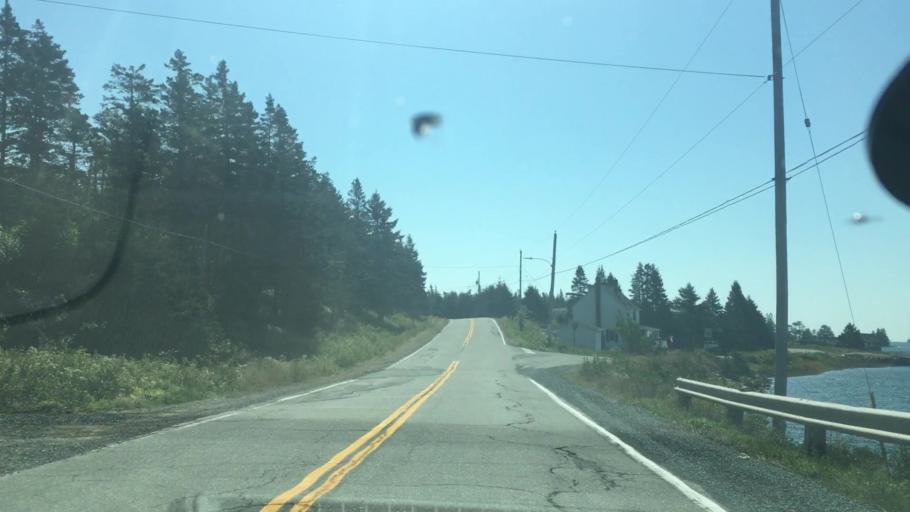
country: CA
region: Nova Scotia
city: New Glasgow
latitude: 44.9131
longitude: -62.3800
